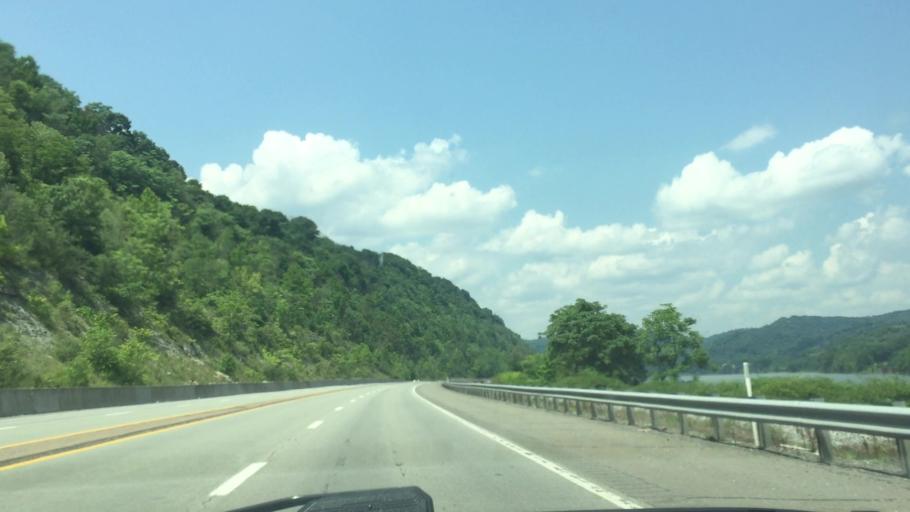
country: US
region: West Virginia
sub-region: Marshall County
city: Moundsville
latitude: 39.9061
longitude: -80.7674
